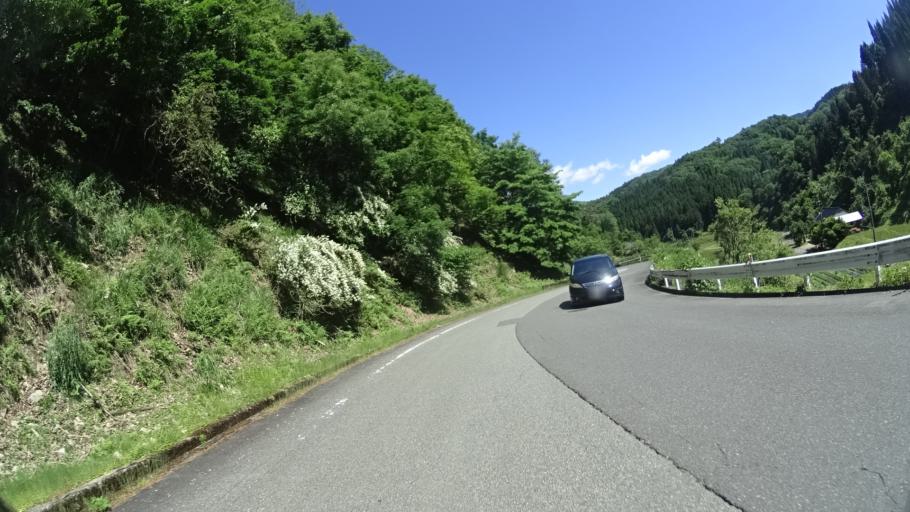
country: JP
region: Kyoto
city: Fukuchiyama
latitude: 35.4260
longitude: 135.0575
